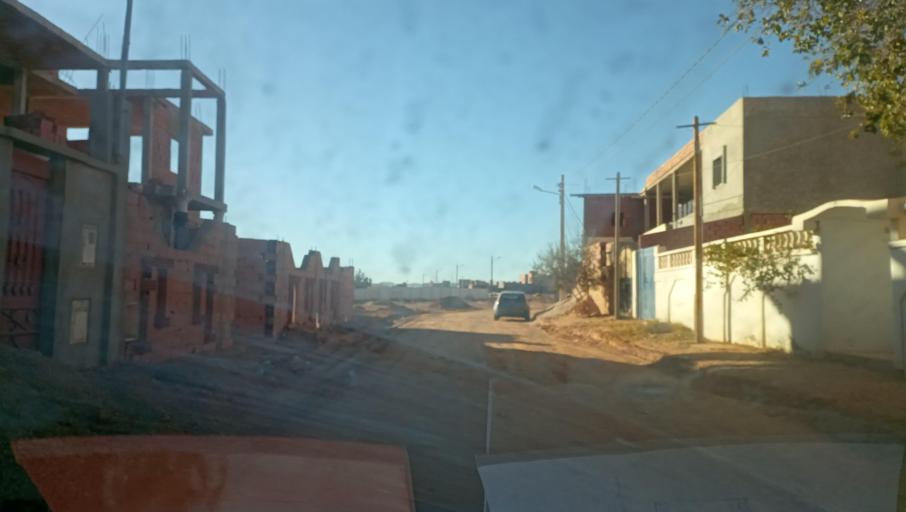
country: TN
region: Tataouine
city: Tataouine
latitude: 32.9868
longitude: 10.4597
